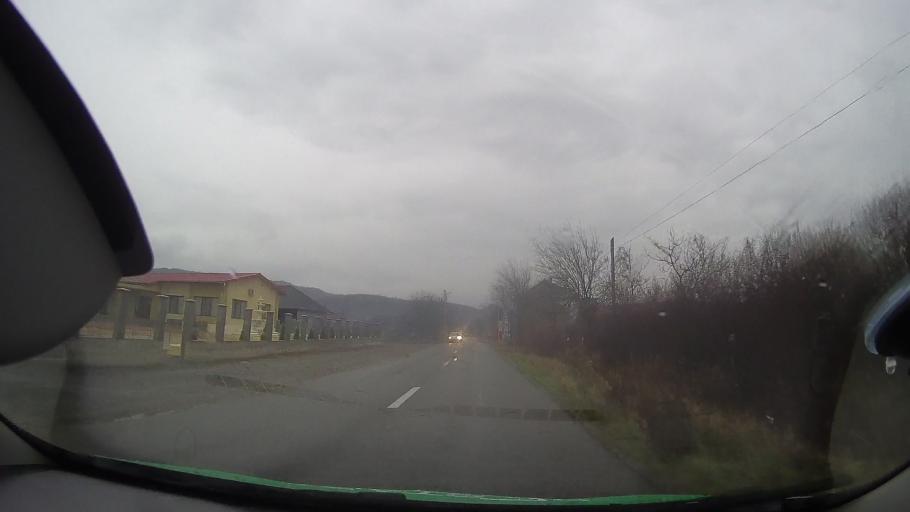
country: RO
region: Bihor
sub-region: Comuna Uileacu de Beius
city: Uileacu de Beius
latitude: 46.6799
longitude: 22.2288
